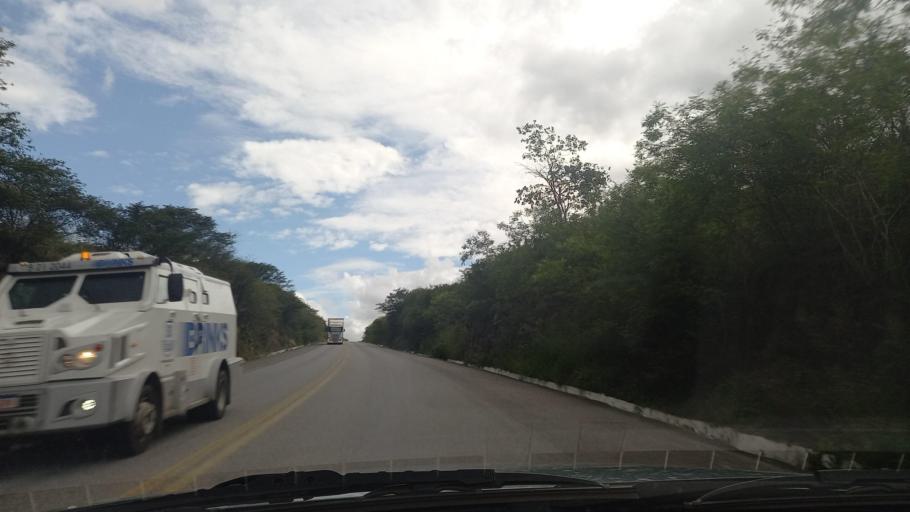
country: BR
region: Pernambuco
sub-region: Lajedo
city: Lajedo
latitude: -8.6742
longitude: -36.3995
